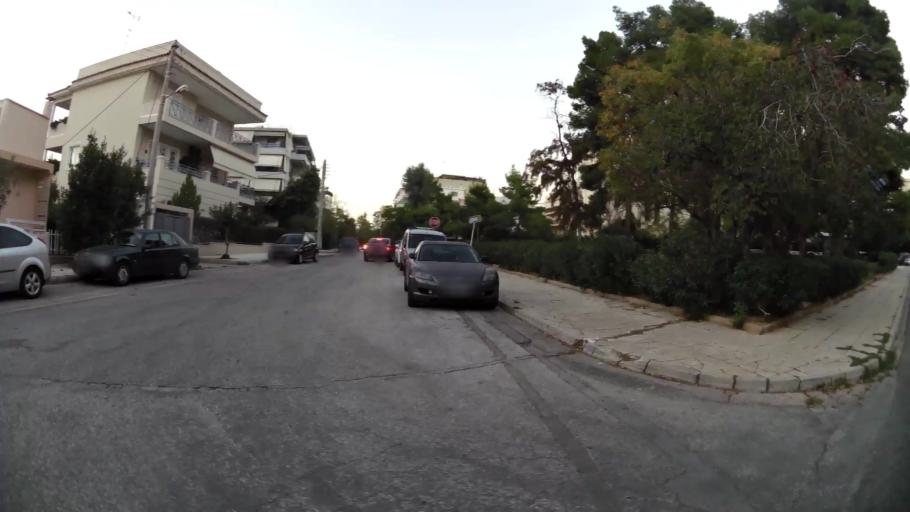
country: GR
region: Attica
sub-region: Nomarchia Athinas
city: Argyroupoli
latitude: 37.8891
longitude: 23.7550
